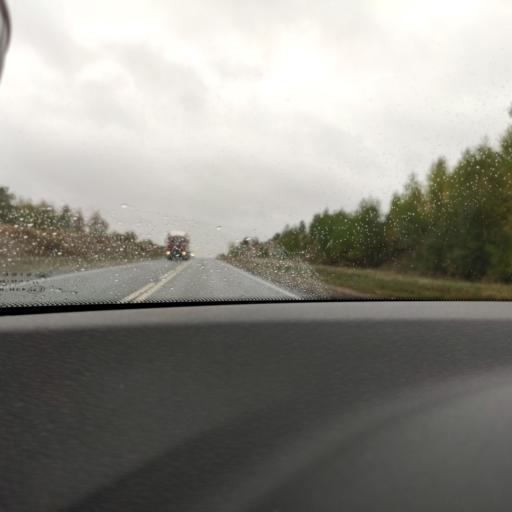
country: RU
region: Samara
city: Mirnyy
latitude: 53.6425
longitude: 50.2232
